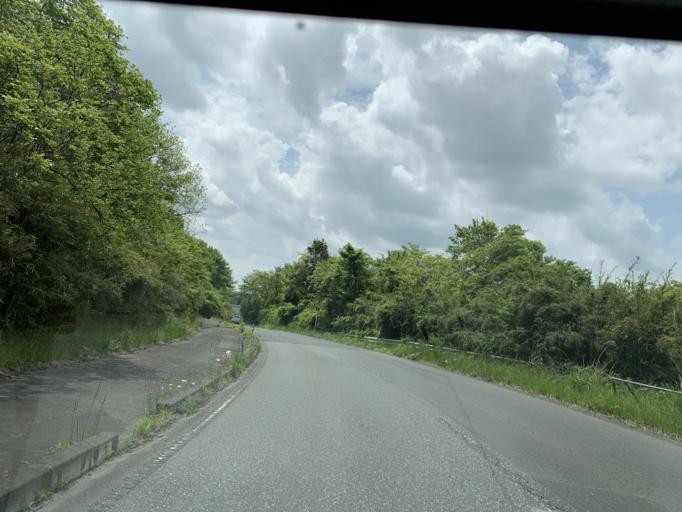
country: JP
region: Miyagi
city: Furukawa
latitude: 38.7009
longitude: 140.9267
